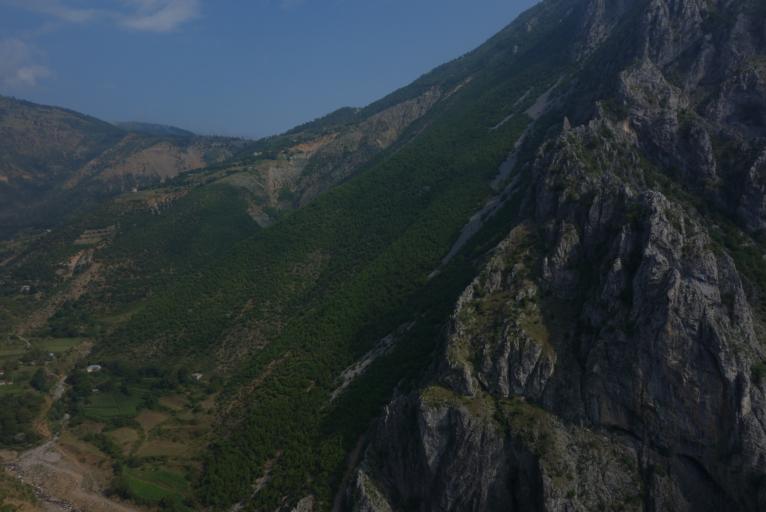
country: AL
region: Diber
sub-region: Rrethi i Dibres
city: Fushe-Lure
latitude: 41.7611
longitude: 20.2362
